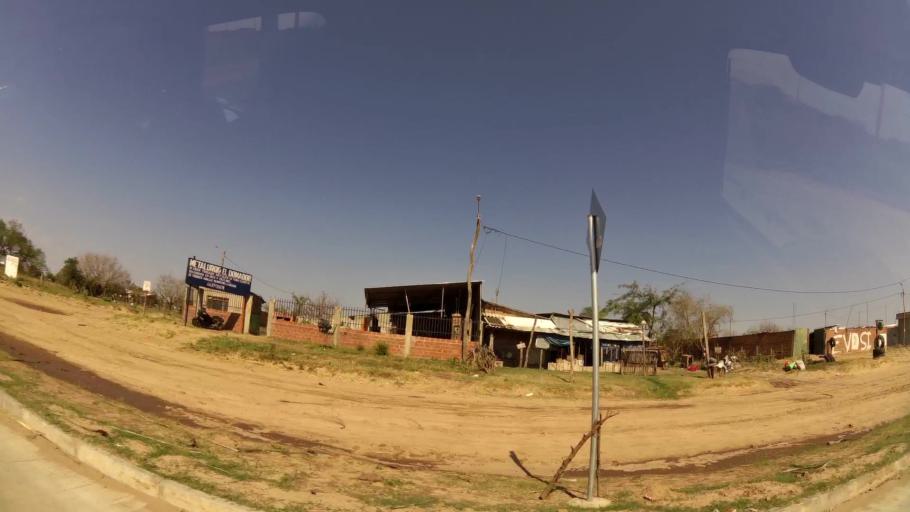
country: BO
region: Santa Cruz
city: Cotoca
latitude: -17.7211
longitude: -63.0759
